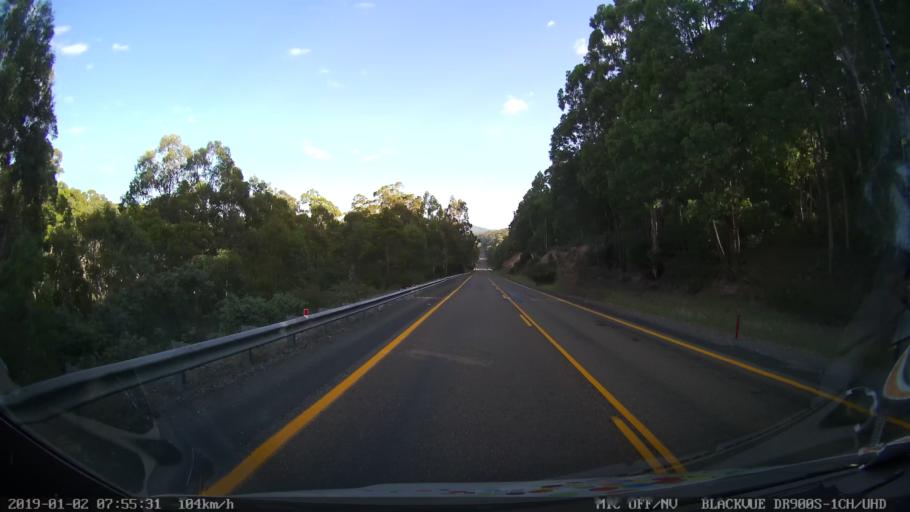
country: AU
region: New South Wales
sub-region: Tumut Shire
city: Tumut
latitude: -35.6836
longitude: 148.4868
